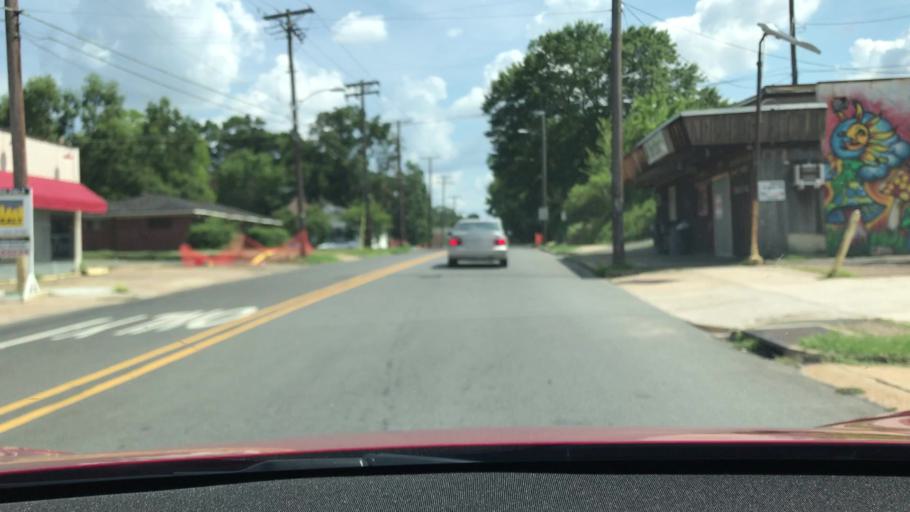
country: US
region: Louisiana
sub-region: Bossier Parish
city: Bossier City
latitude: 32.4998
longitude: -93.7332
